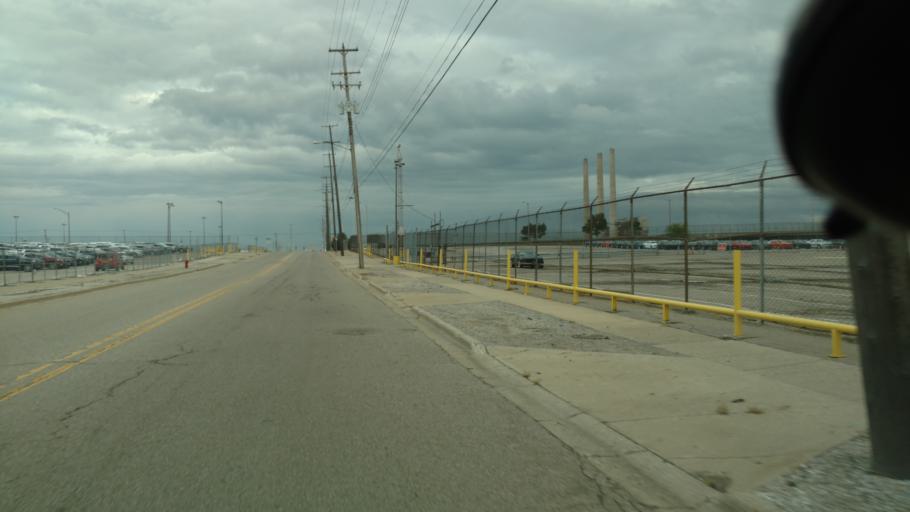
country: US
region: Michigan
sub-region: Ingham County
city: Lansing
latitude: 42.7233
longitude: -84.5717
